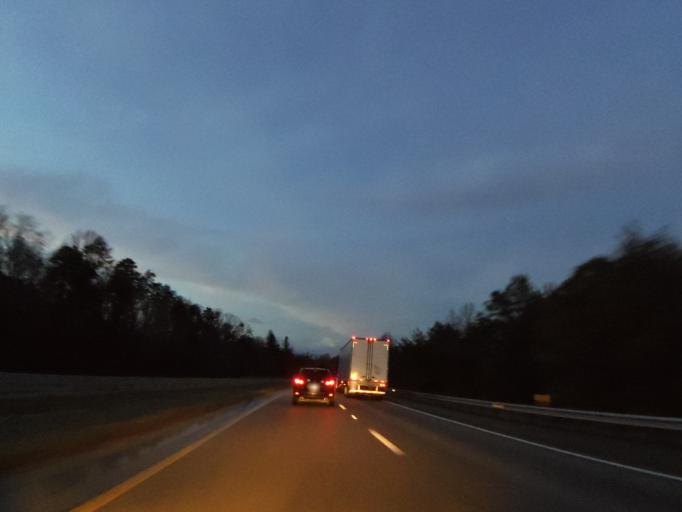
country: US
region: Kentucky
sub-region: Whitley County
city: Corbin
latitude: 36.8814
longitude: -84.1507
